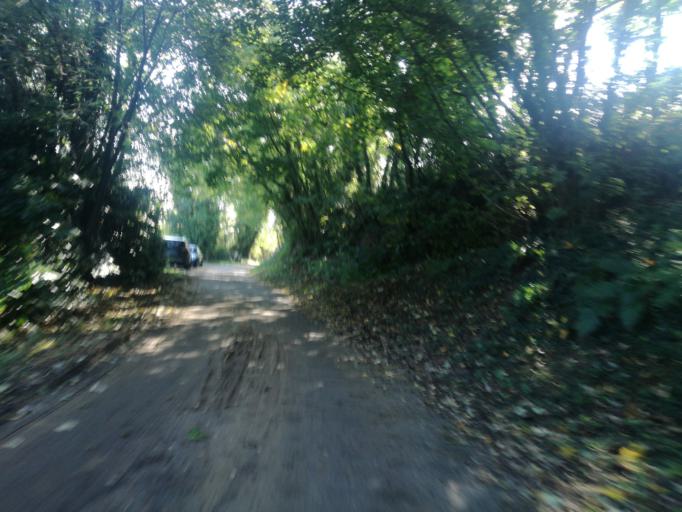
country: IT
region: Lombardy
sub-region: Provincia di Bergamo
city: Bottanuco
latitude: 45.6224
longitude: 9.5092
